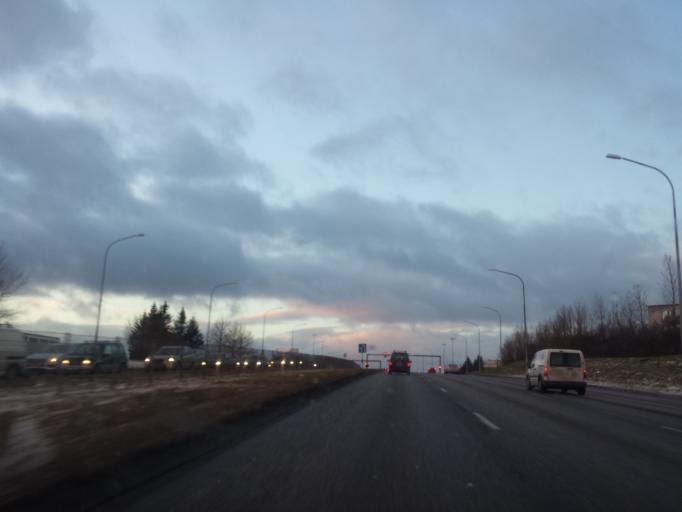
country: IS
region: Capital Region
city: Reykjavik
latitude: 64.1303
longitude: -21.8795
